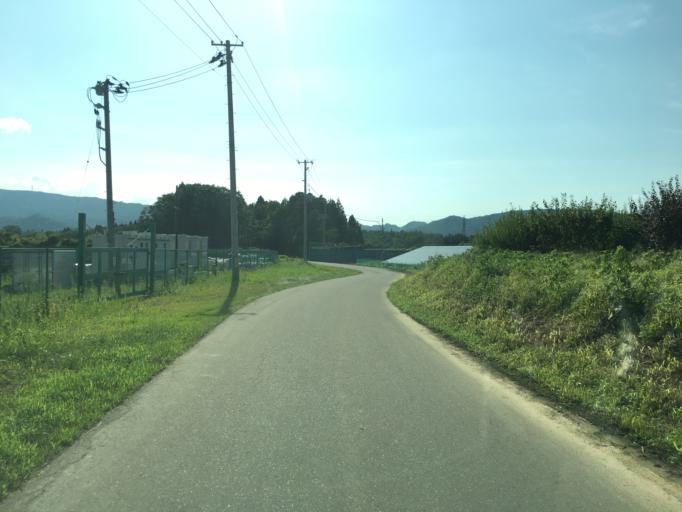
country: JP
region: Miyagi
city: Marumori
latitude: 37.8235
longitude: 140.9064
